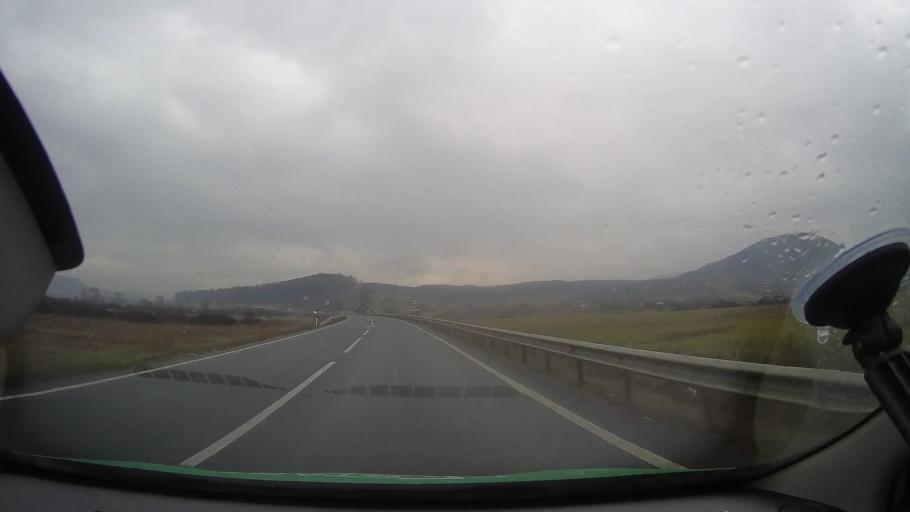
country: RO
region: Hunedoara
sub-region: Comuna Baia de Cris
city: Baia de Cris
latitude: 46.1787
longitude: 22.6846
